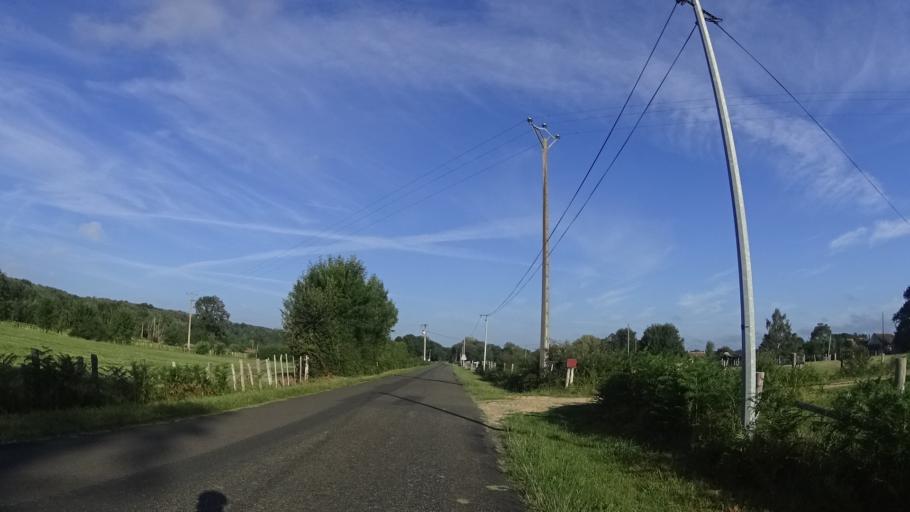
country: FR
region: Pays de la Loire
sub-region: Departement de la Sarthe
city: Bazouges-sur-le-Loir
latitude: 47.6806
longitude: -0.1218
